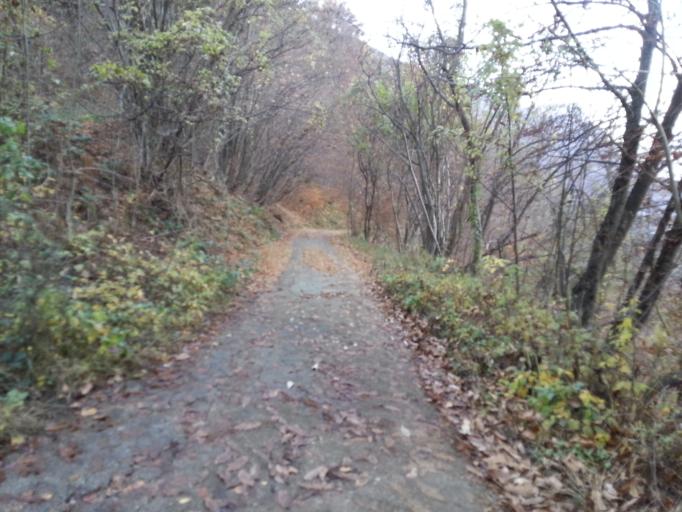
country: IT
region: Lombardy
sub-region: Provincia di Lecco
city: Primaluna
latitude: 45.9766
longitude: 9.4217
